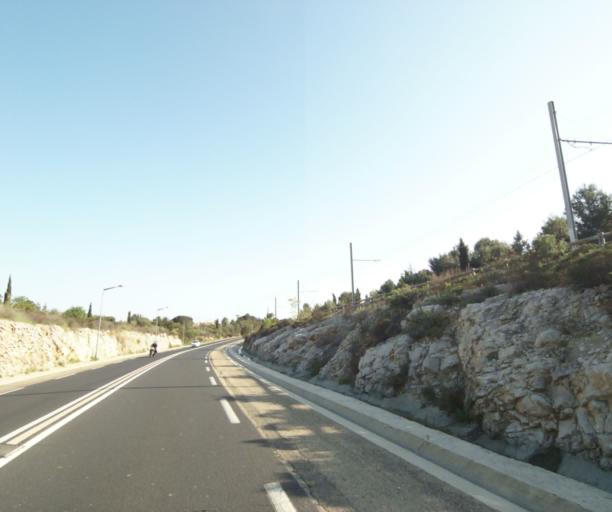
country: FR
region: Languedoc-Roussillon
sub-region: Departement de l'Herault
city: Le Cres
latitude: 43.6449
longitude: 3.9308
